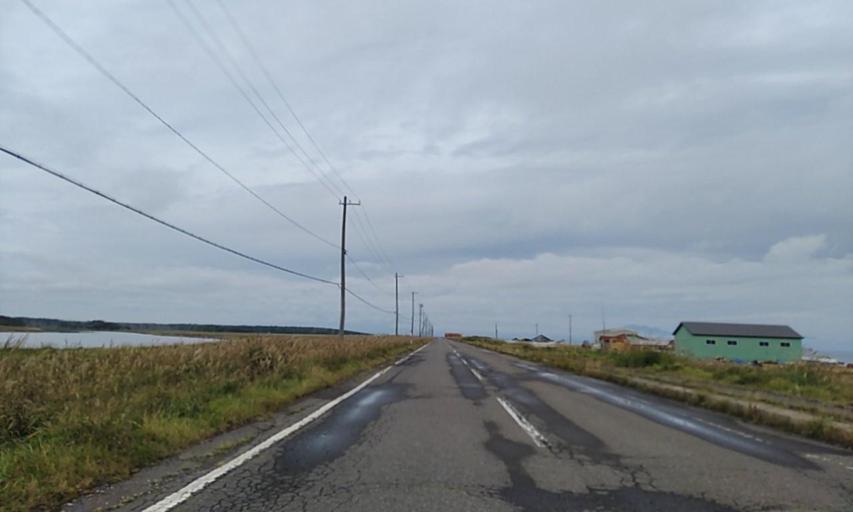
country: JP
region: Hokkaido
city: Shibetsu
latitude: 43.6000
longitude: 145.3112
